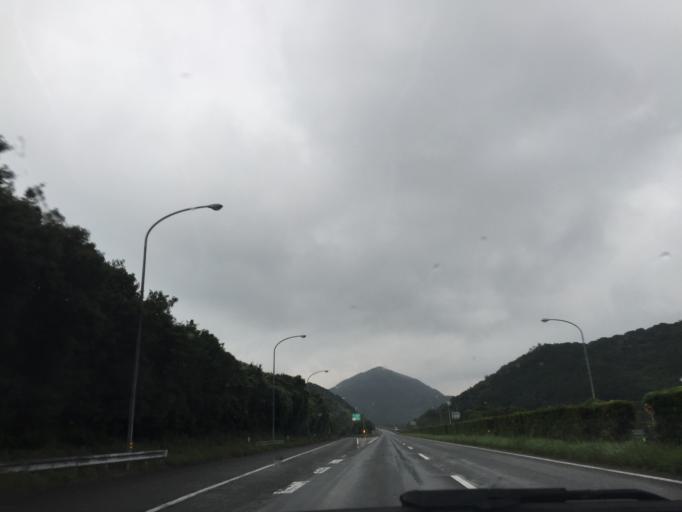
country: JP
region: Tokushima
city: Narutocho-mitsuishi
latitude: 34.2237
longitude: 134.6281
